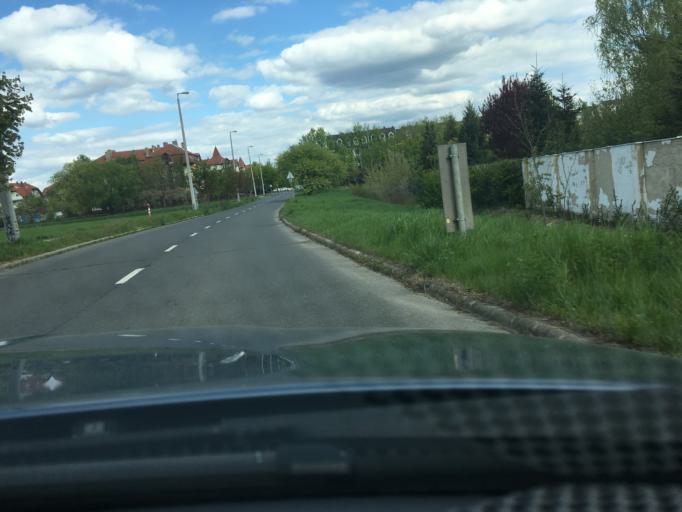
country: HU
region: Hajdu-Bihar
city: Debrecen
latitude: 47.5552
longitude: 21.5951
